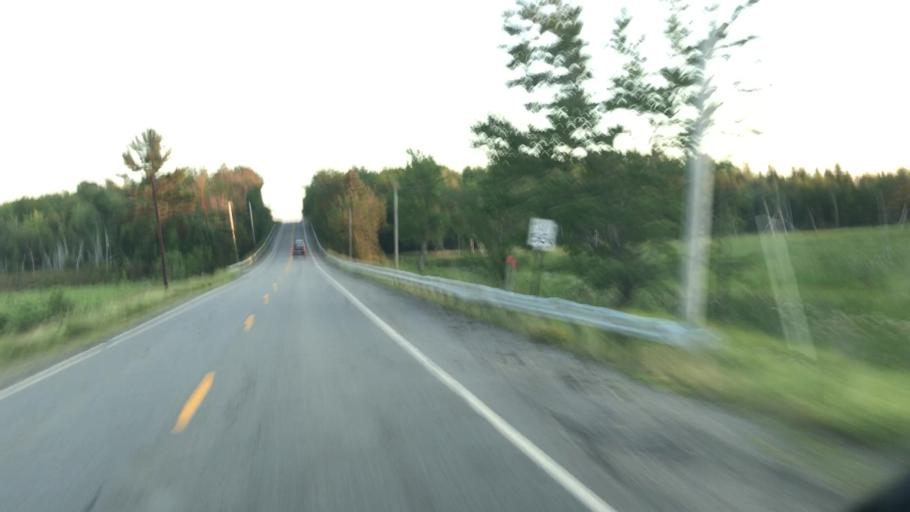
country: US
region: Maine
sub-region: Penobscot County
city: Medway
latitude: 45.5984
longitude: -68.3102
